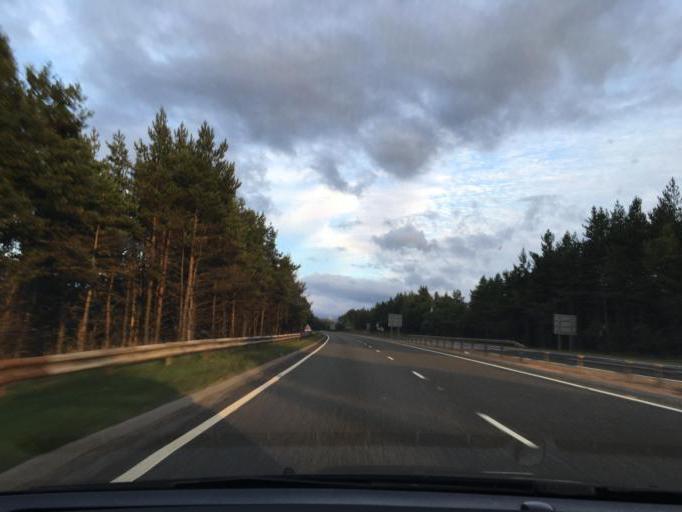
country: GB
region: Scotland
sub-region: Highland
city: Aviemore
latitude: 57.3425
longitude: -3.9963
